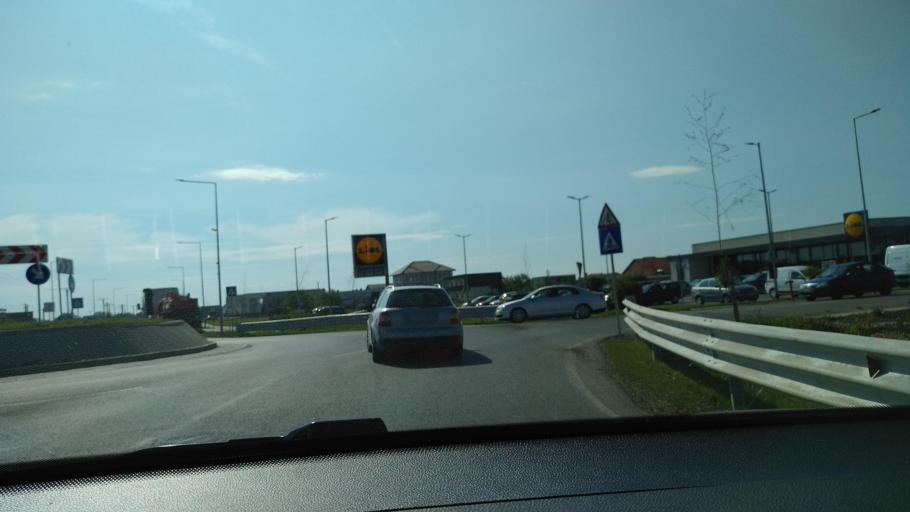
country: RO
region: Timis
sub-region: Comuna Mosnita Noua
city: Mosnita Noua
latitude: 45.7229
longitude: 21.2992
